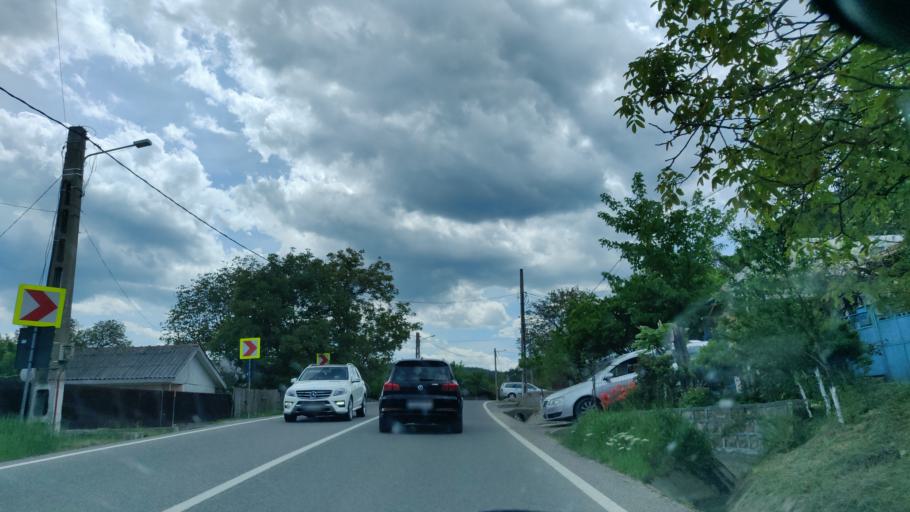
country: RO
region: Vrancea
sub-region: Comuna Tulnici
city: Tulnici
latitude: 45.9139
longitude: 26.6687
